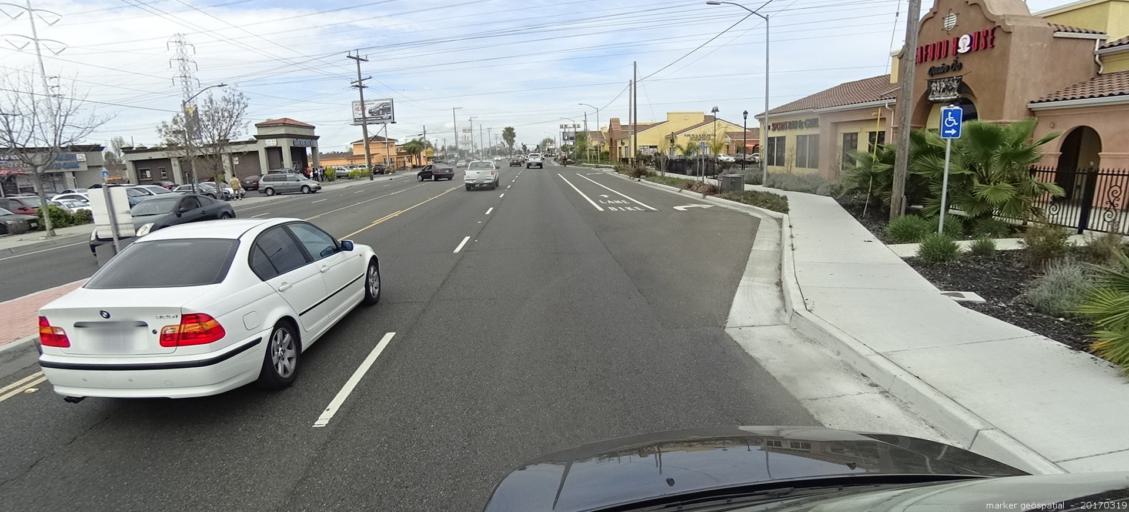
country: US
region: California
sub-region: Sacramento County
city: Parkway
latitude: 38.5079
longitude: -121.4346
